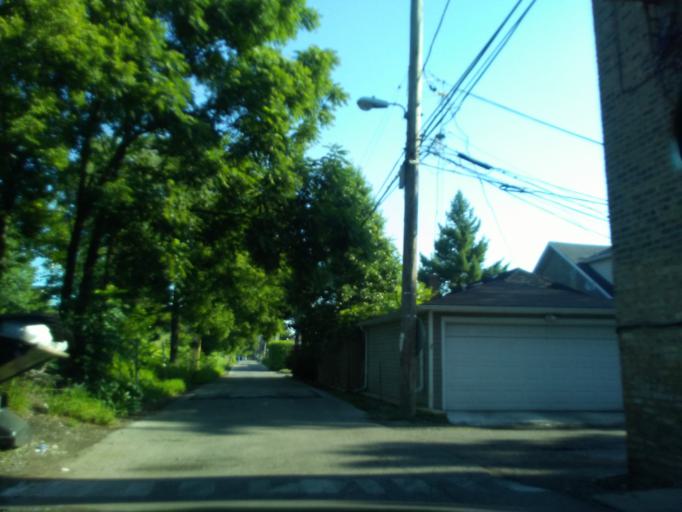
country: US
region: Illinois
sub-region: Cook County
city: Oak Park
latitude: 41.9347
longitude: -87.7417
